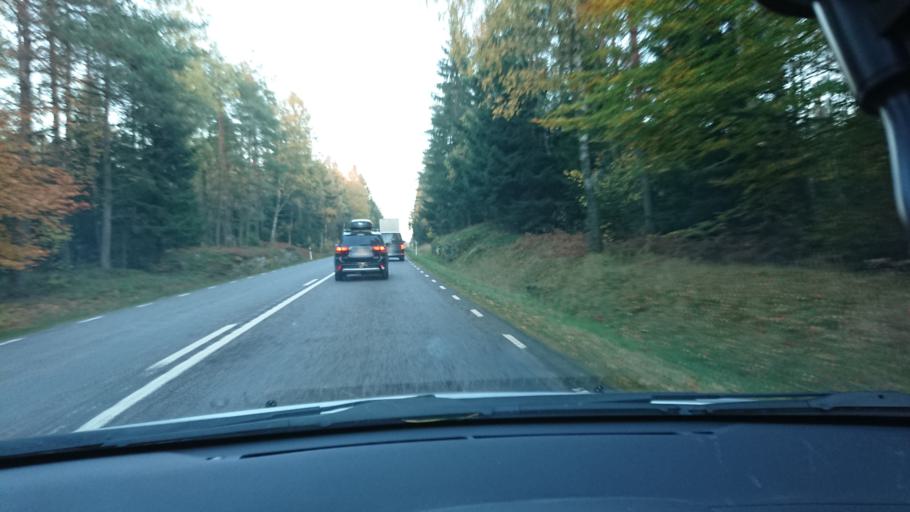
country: SE
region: Halland
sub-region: Laholms Kommun
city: Veinge
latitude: 56.7190
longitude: 13.1790
